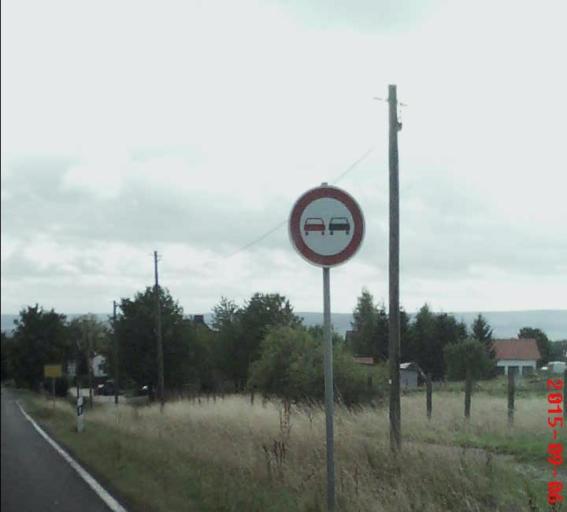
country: DE
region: Thuringia
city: Sollstedt
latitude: 51.2940
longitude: 10.4456
